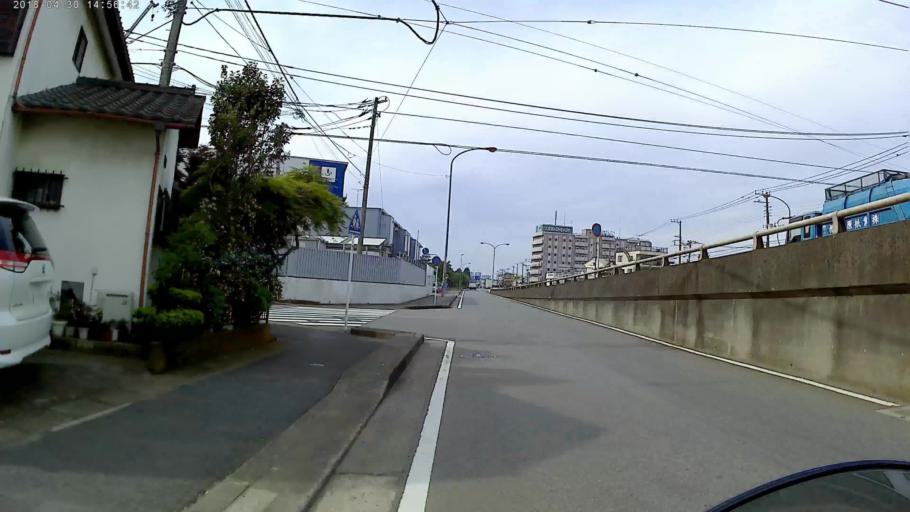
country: JP
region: Kanagawa
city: Zama
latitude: 35.5574
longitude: 139.3476
